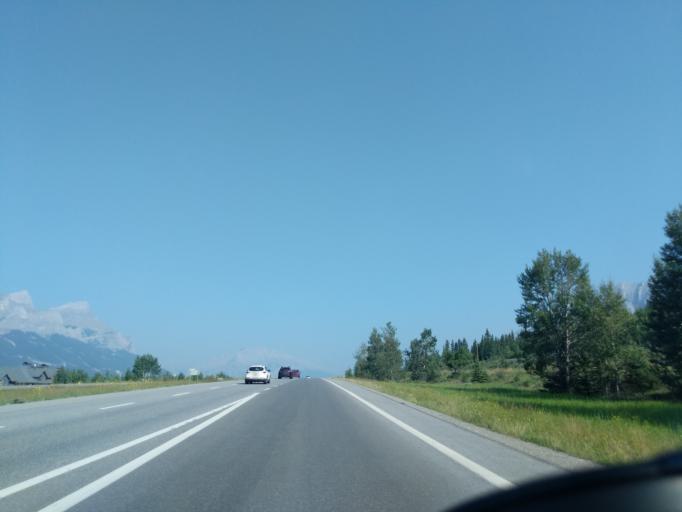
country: CA
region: Alberta
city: Canmore
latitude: 51.0995
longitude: -115.3554
